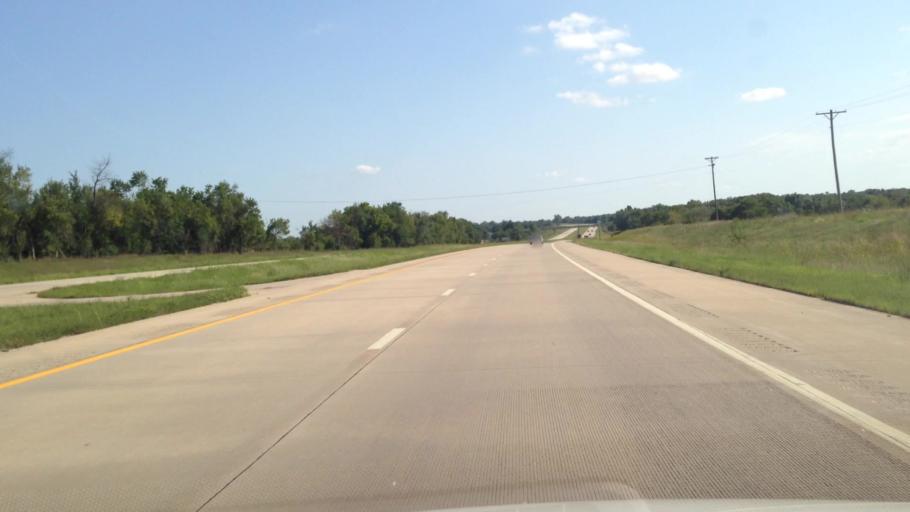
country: US
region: Kansas
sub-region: Bourbon County
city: Fort Scott
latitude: 37.8876
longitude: -94.7040
